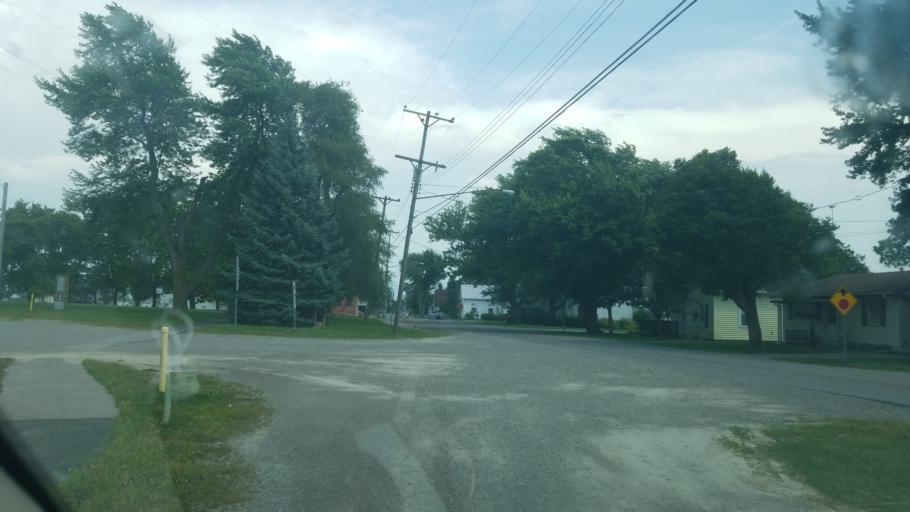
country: US
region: Ohio
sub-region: Logan County
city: Northwood
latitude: 40.4630
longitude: -83.6744
